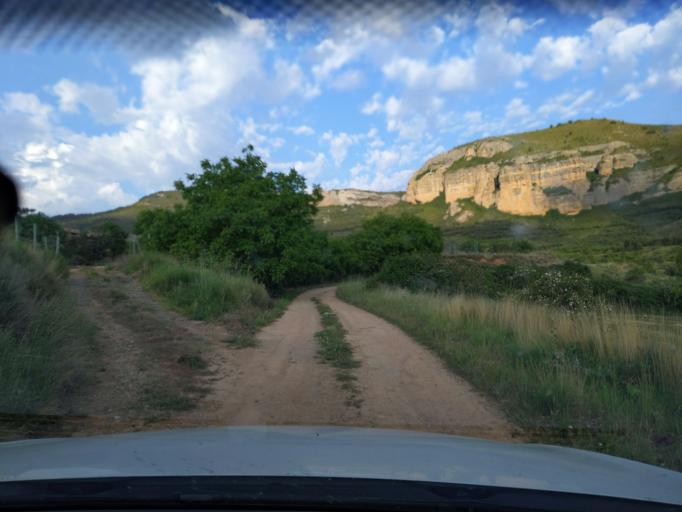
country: ES
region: La Rioja
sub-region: Provincia de La Rioja
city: Nalda
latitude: 42.3279
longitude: -2.4772
